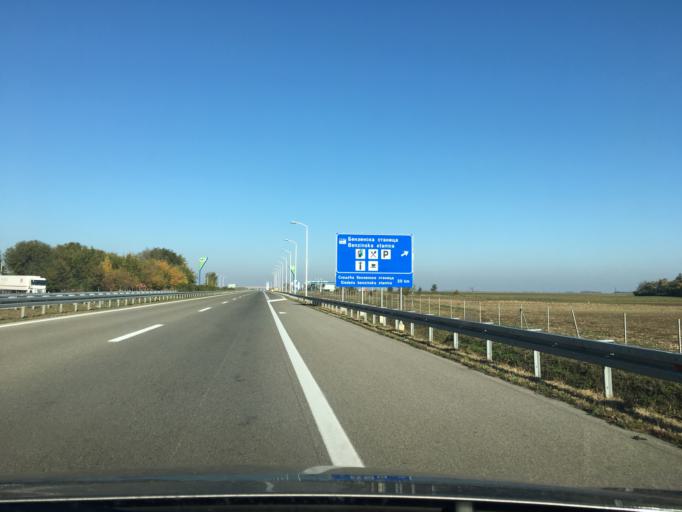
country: RS
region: Autonomna Pokrajina Vojvodina
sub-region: Severnobacki Okrug
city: Backa Topola
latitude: 45.7912
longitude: 19.6949
